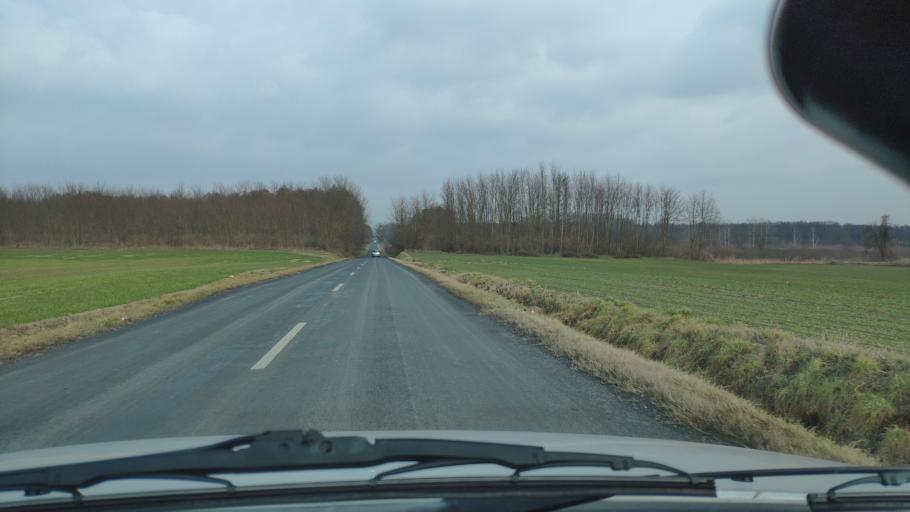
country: HU
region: Zala
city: Nagykanizsa
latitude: 46.4417
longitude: 16.9229
